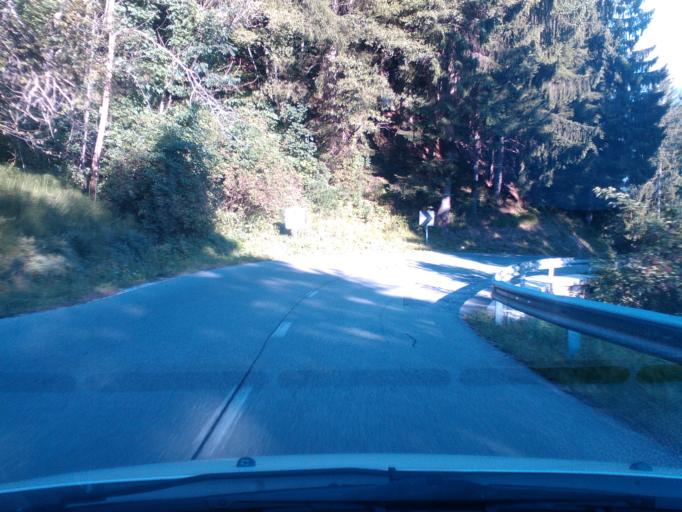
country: SI
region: Kranjska Gora
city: Kranjska Gora
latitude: 46.4996
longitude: 13.7569
